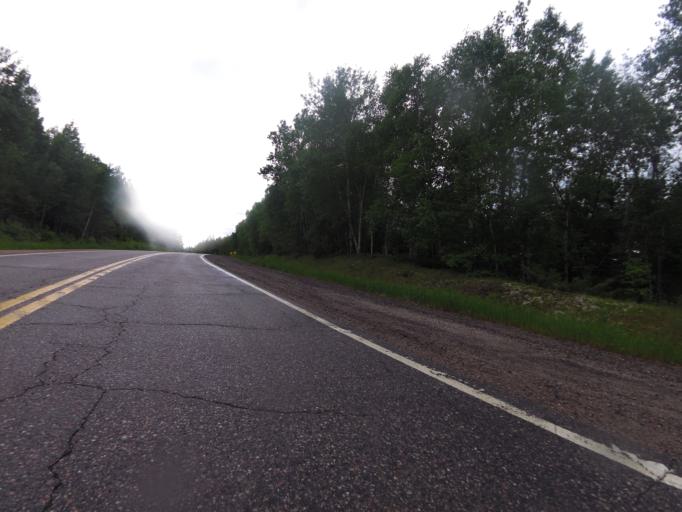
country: CA
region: Quebec
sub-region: Outaouais
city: Shawville
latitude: 45.9060
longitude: -76.2784
